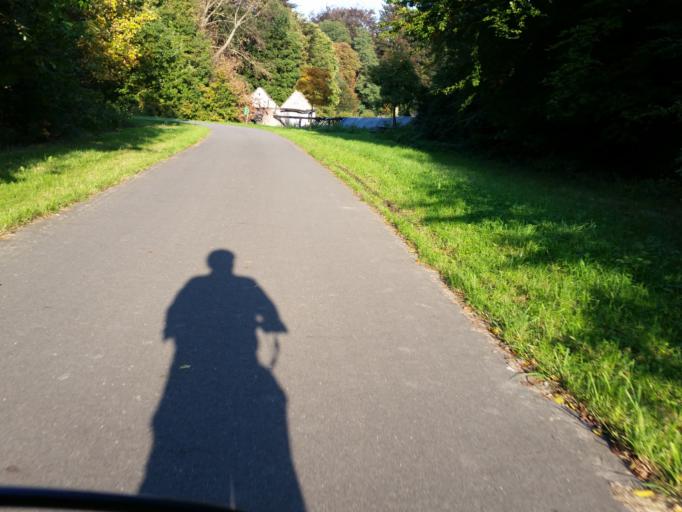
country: BE
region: Flanders
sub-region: Provincie Antwerpen
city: Niel
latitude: 51.1200
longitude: 4.3113
